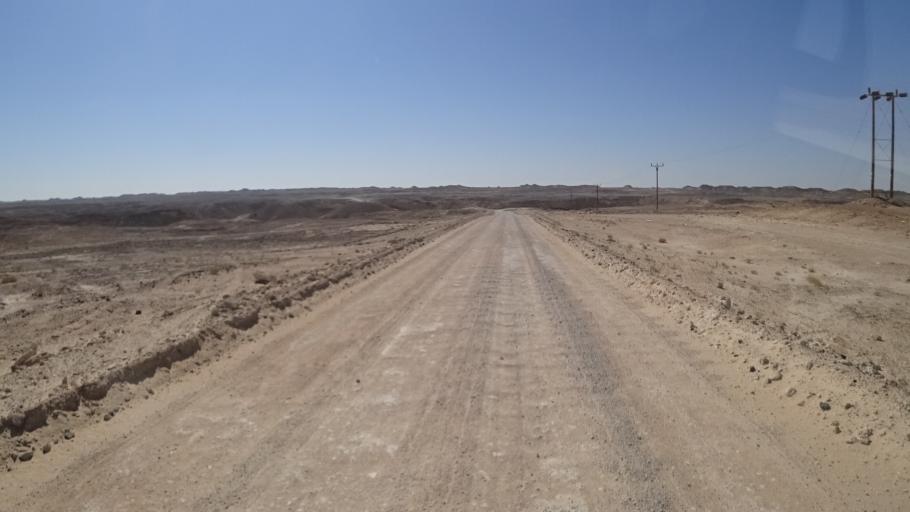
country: YE
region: Al Mahrah
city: Hawf
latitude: 17.3746
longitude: 53.2001
